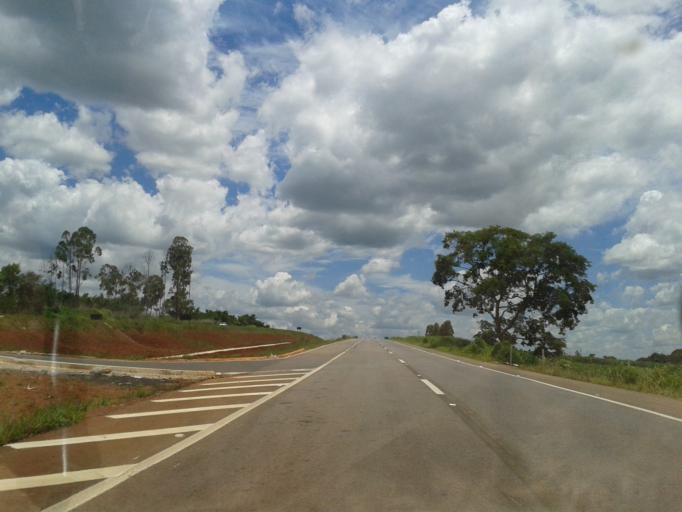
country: BR
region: Goias
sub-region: Neropolis
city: Neropolis
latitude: -16.3739
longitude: -49.2274
